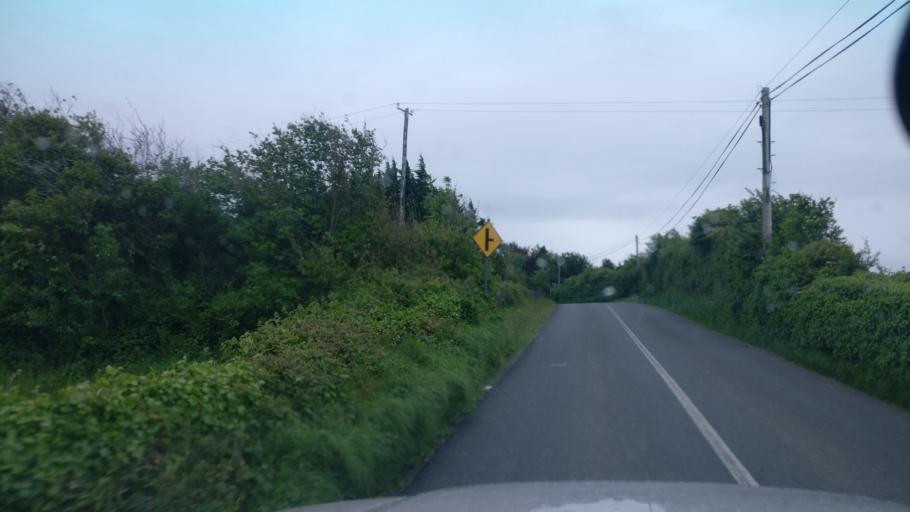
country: IE
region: Connaught
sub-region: County Galway
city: Gort
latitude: 53.0683
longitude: -8.7816
